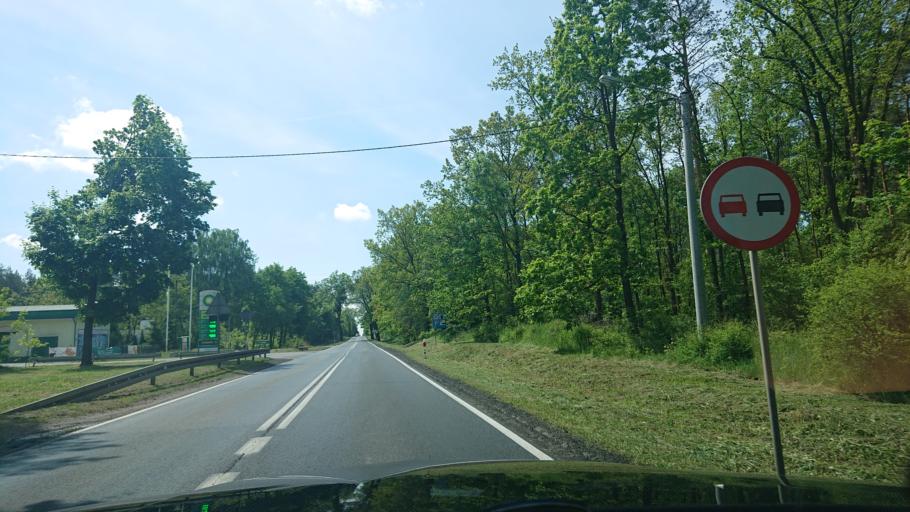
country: PL
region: Greater Poland Voivodeship
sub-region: Powiat gnieznienski
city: Gniezno
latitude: 52.4932
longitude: 17.5940
